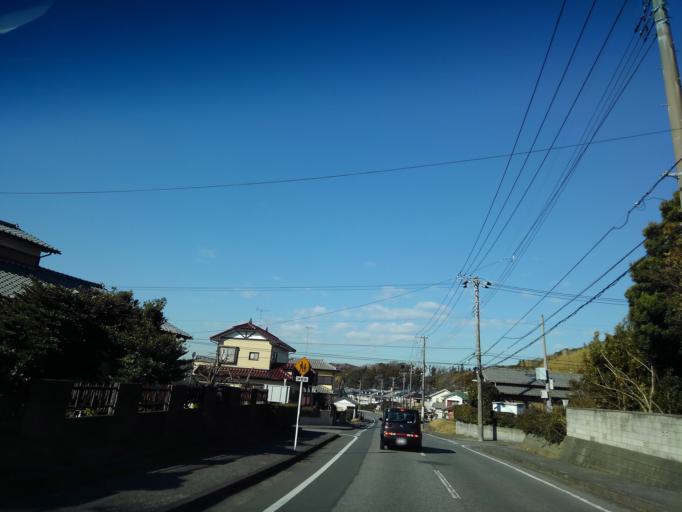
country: JP
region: Chiba
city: Kimitsu
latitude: 35.3337
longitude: 139.9219
